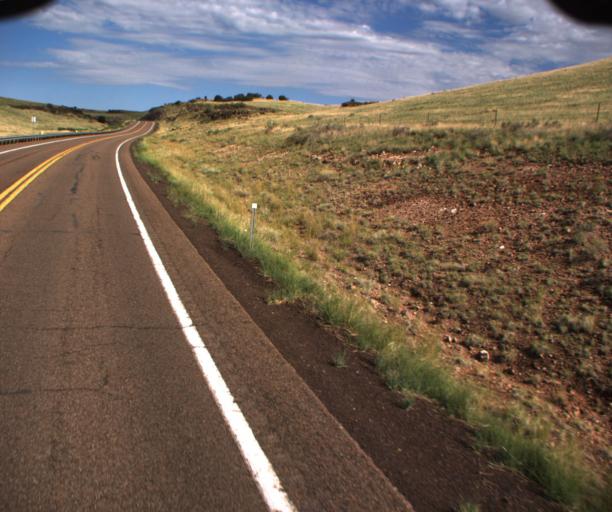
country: US
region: Arizona
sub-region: Apache County
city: Springerville
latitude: 34.2083
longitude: -109.4240
